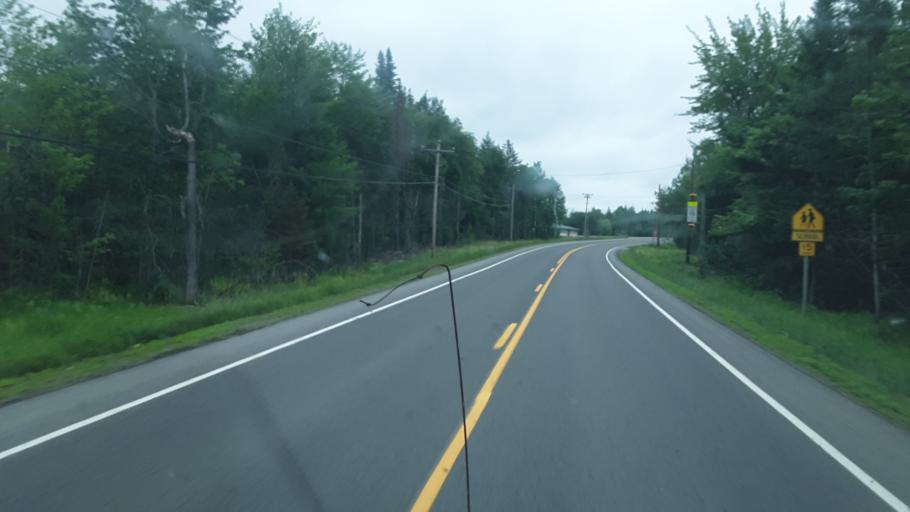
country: US
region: Maine
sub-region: Penobscot County
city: Patten
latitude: 45.9270
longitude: -68.4413
